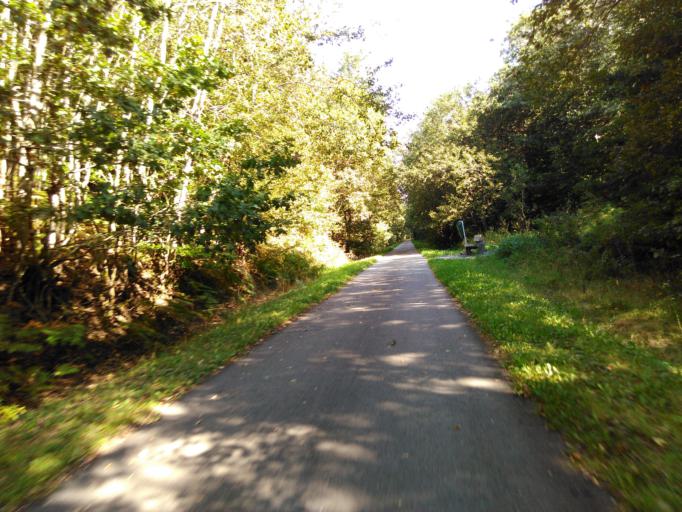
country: BE
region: Wallonia
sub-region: Province du Luxembourg
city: Bastogne
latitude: 50.0398
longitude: 5.7771
